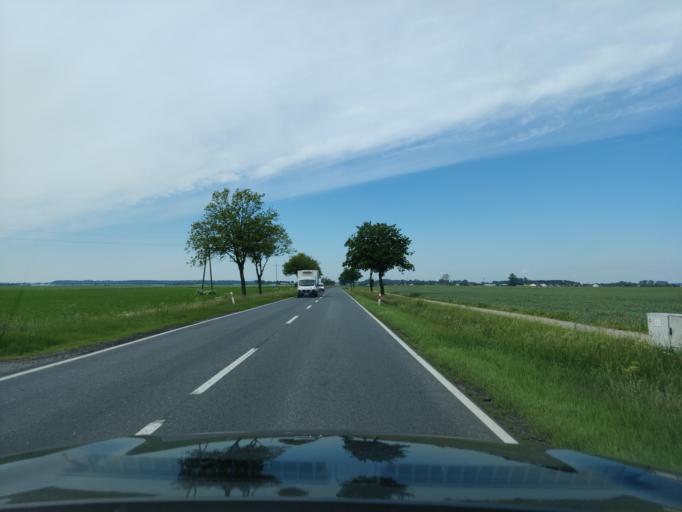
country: PL
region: Greater Poland Voivodeship
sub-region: Powiat poznanski
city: Steszew
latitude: 52.2534
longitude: 16.6377
